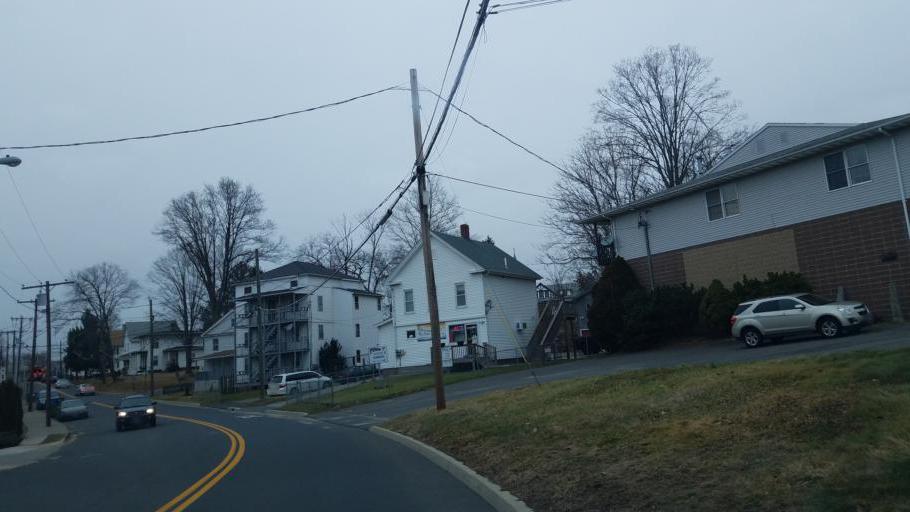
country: US
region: Connecticut
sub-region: Middlesex County
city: Middletown
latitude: 41.5498
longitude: -72.6398
